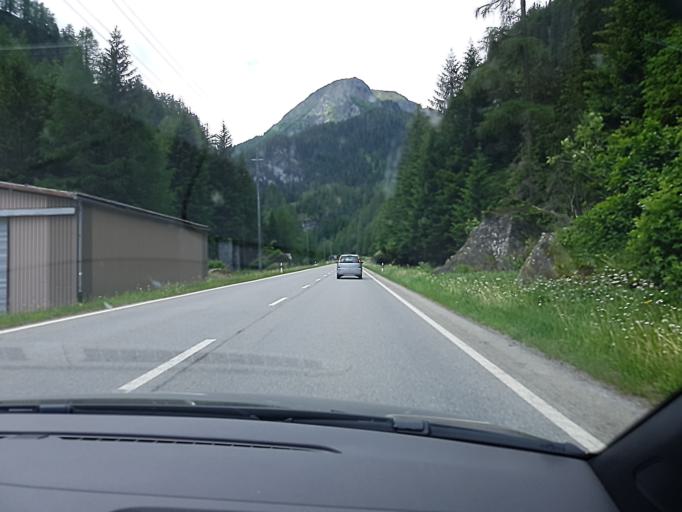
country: CH
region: Grisons
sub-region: Albula District
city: Tiefencastel
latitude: 46.5316
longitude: 9.6221
